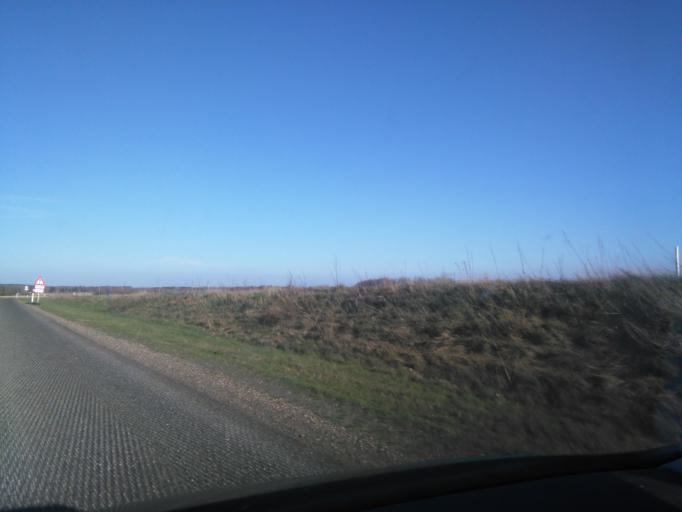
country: DK
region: Central Jutland
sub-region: Ringkobing-Skjern Kommune
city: Videbaek
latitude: 56.0988
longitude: 8.6255
